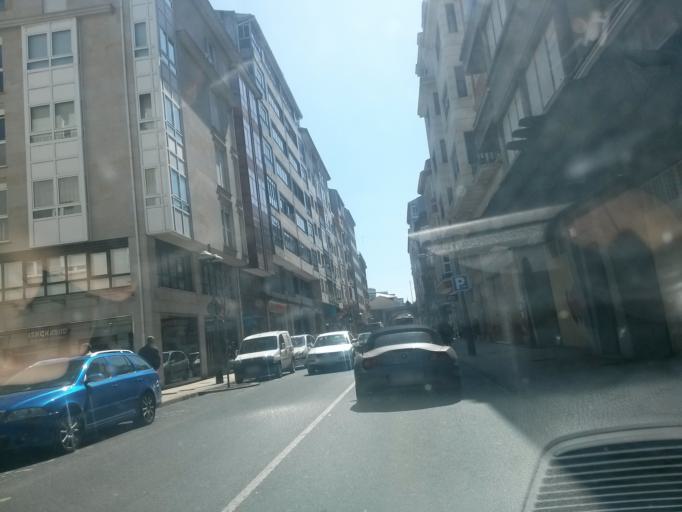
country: ES
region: Galicia
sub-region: Provincia de Lugo
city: Lugo
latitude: 43.0162
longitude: -7.5598
